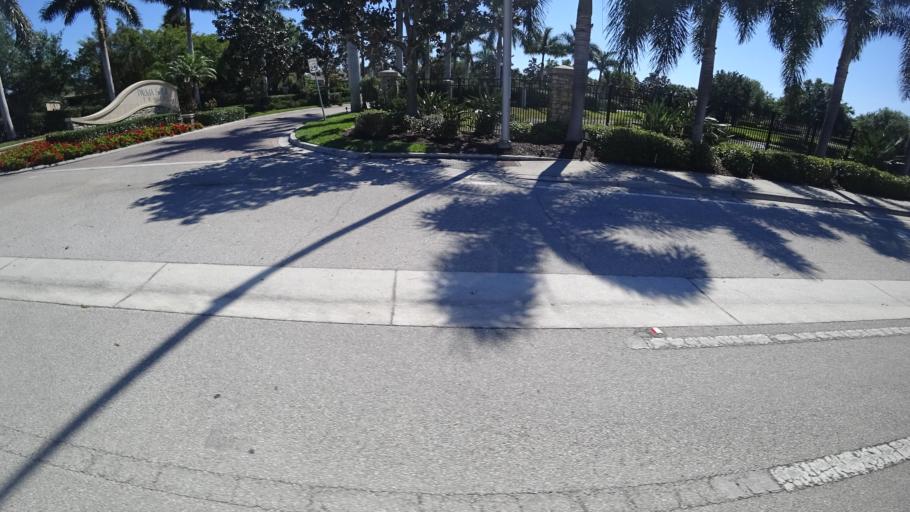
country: US
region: Florida
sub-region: Manatee County
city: West Bradenton
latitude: 27.4700
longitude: -82.6368
